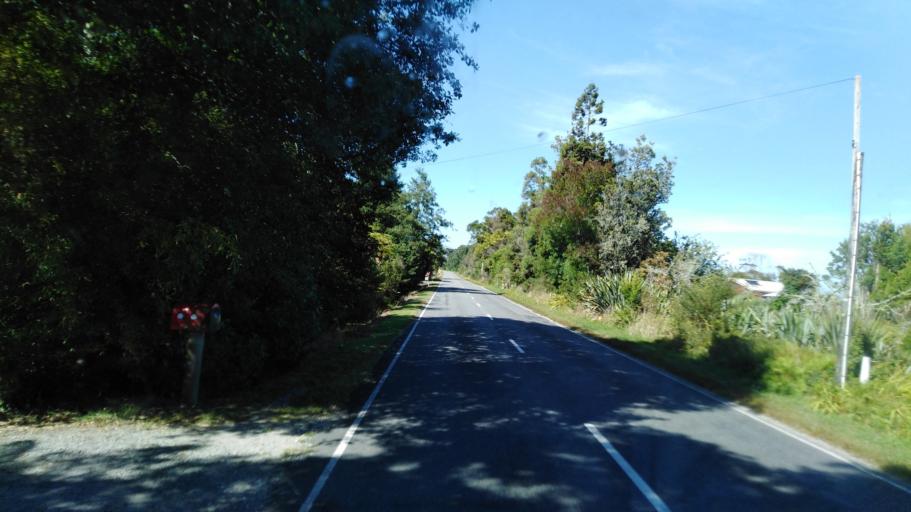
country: NZ
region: West Coast
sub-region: Buller District
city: Westport
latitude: -41.2732
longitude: 172.1094
